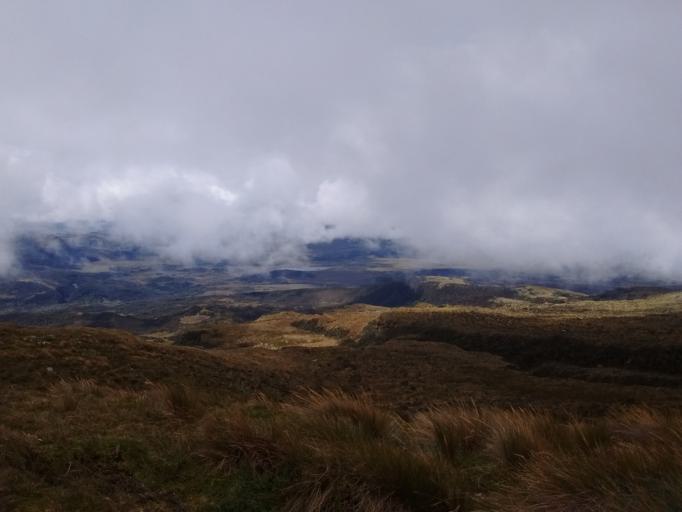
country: CO
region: Cauca
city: Totoro
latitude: 2.3307
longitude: -76.3948
